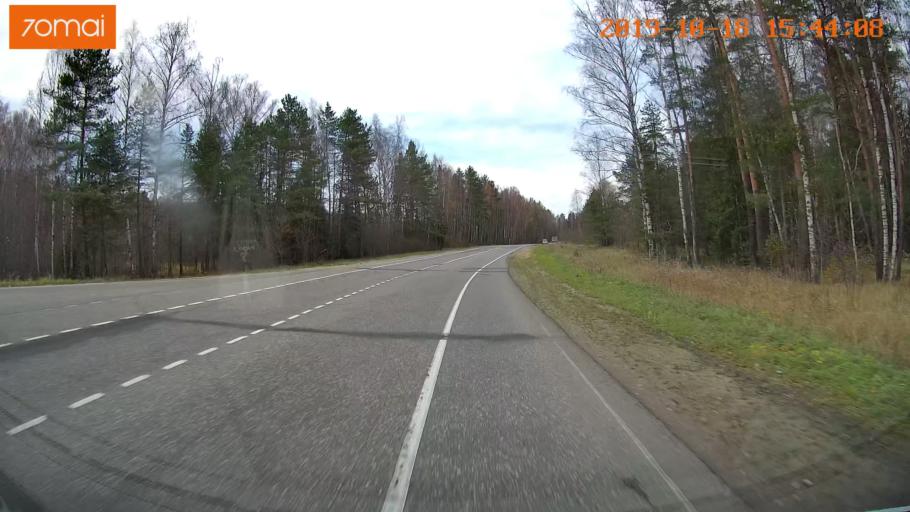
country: RU
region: Vladimir
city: Golovino
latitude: 55.9775
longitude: 40.5471
